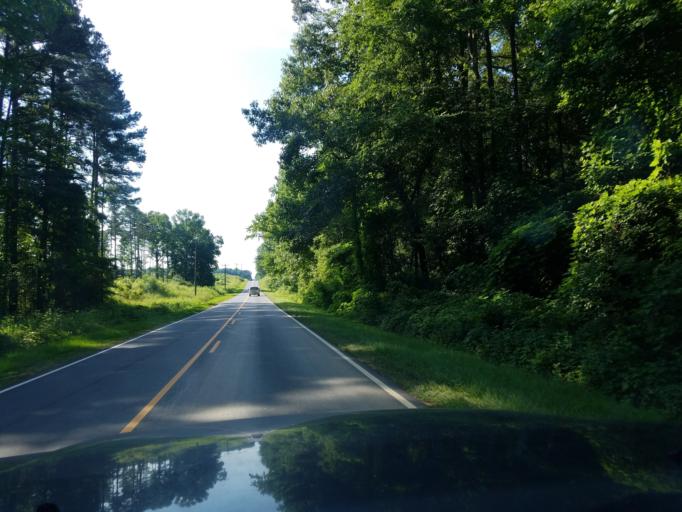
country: US
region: North Carolina
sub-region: Granville County
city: Butner
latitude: 36.1723
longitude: -78.7925
